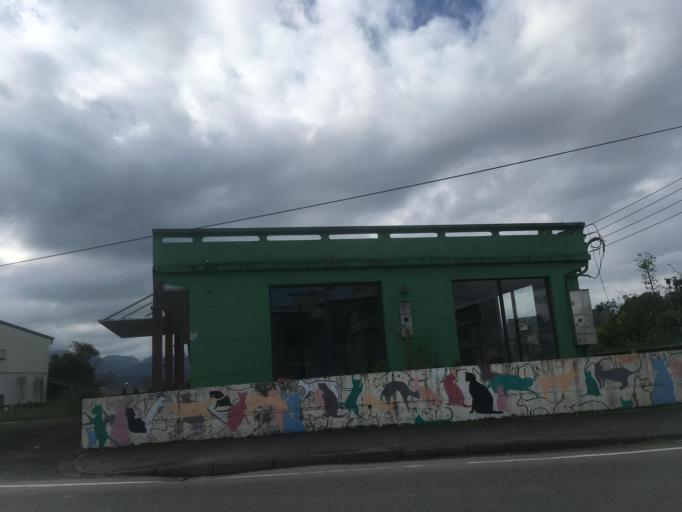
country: TW
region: Taiwan
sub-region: Yilan
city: Yilan
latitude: 24.6870
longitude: 121.7398
